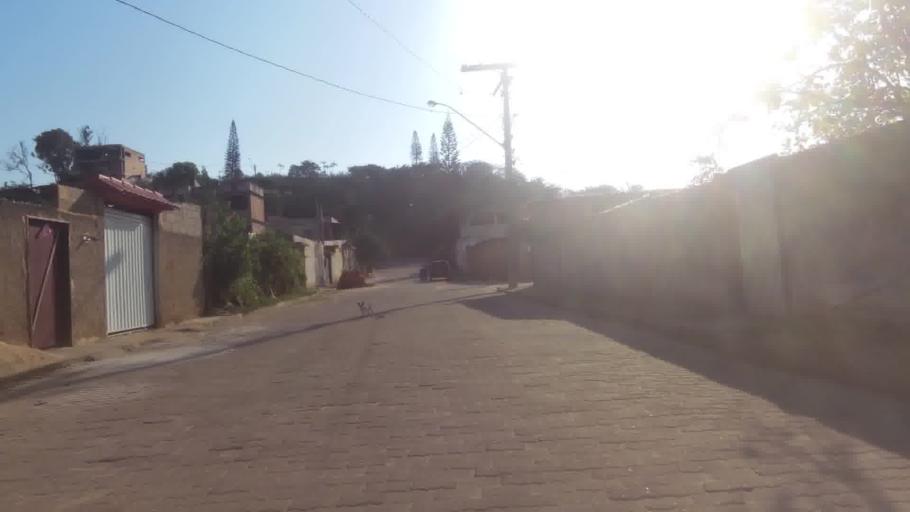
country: BR
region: Espirito Santo
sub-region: Itapemirim
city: Itapemirim
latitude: -21.0183
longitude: -40.8180
